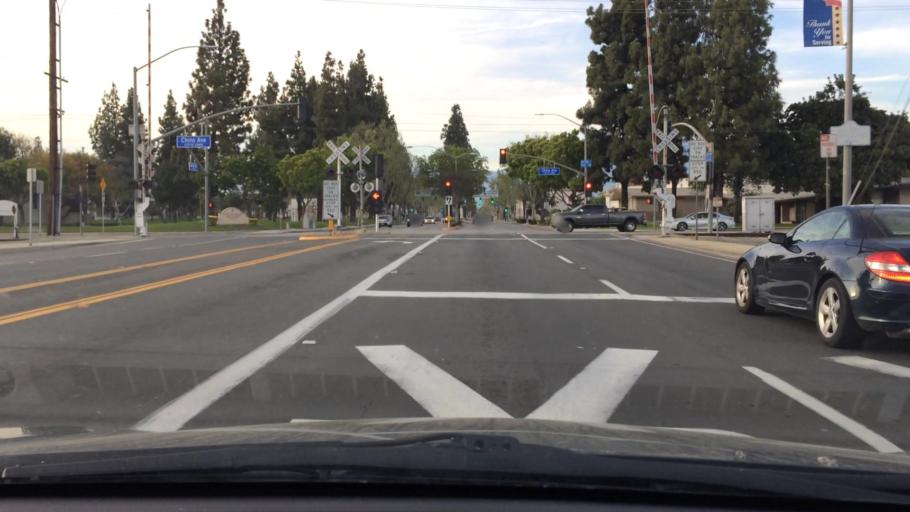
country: US
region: California
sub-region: San Bernardino County
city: Chino
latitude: 34.0114
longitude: -117.6892
